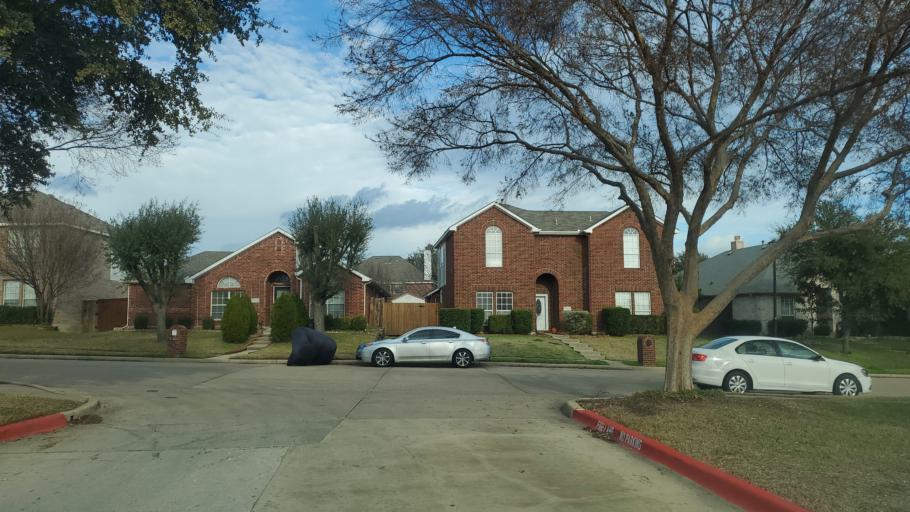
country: US
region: Texas
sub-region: Dallas County
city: Carrollton
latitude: 33.0022
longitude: -96.8944
